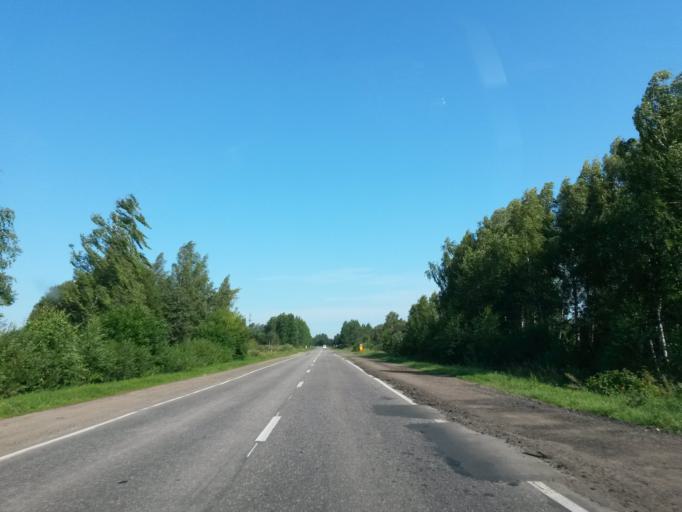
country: RU
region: Jaroslavl
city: Yaroslavl
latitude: 57.5306
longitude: 39.8755
